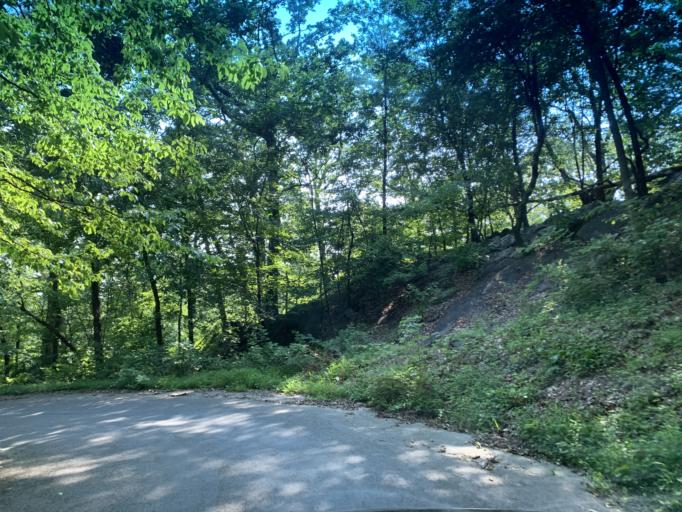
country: US
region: Maryland
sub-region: Frederick County
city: Urbana
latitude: 39.2595
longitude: -77.3978
